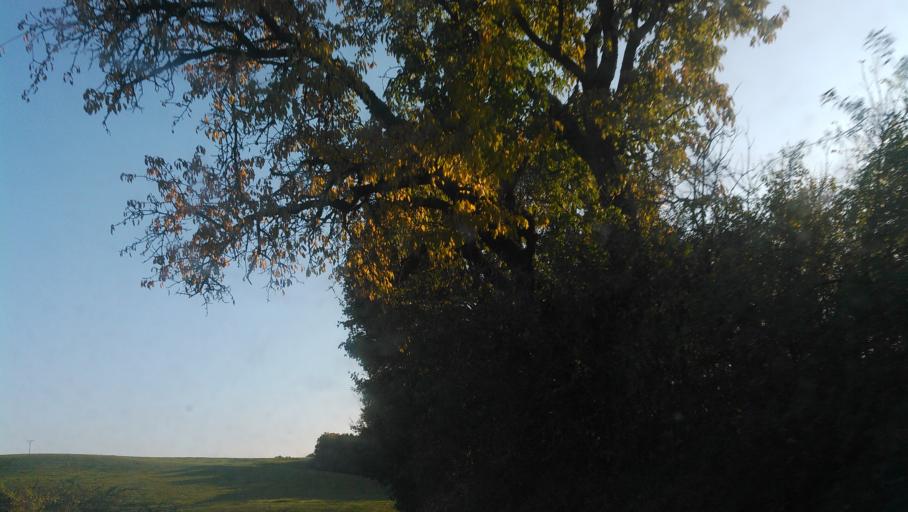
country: SK
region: Trnavsky
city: Hlohovec
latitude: 48.3478
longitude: 17.8778
